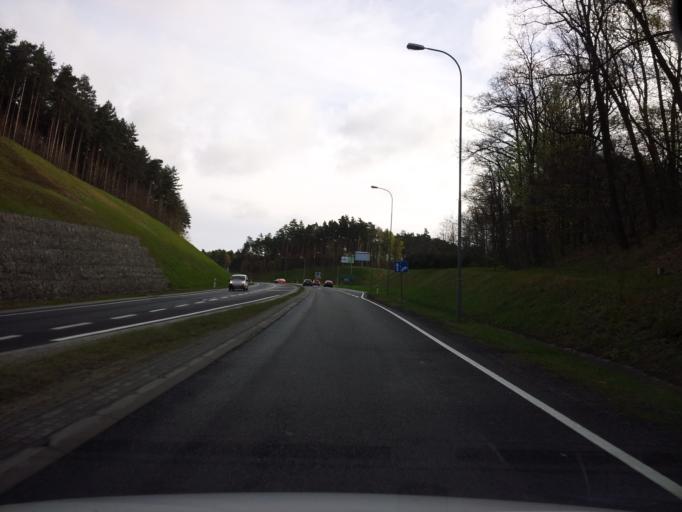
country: PL
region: Lubusz
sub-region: Powiat zielonogorski
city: Swidnica
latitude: 51.9070
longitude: 15.4184
